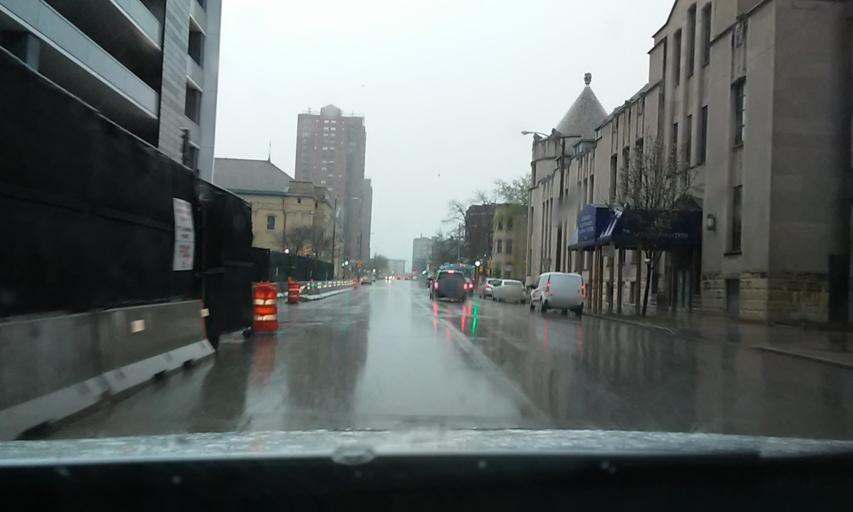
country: US
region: Wisconsin
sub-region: Milwaukee County
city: Milwaukee
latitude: 43.0405
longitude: -87.9030
